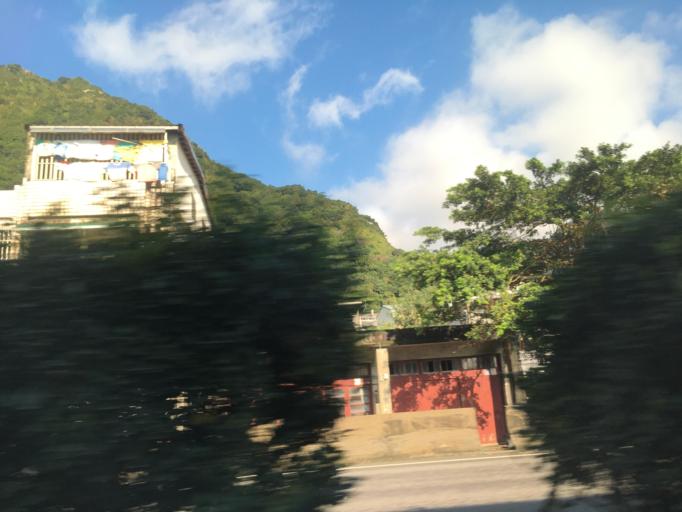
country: TW
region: Taiwan
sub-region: Yilan
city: Yilan
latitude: 24.9401
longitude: 121.8931
